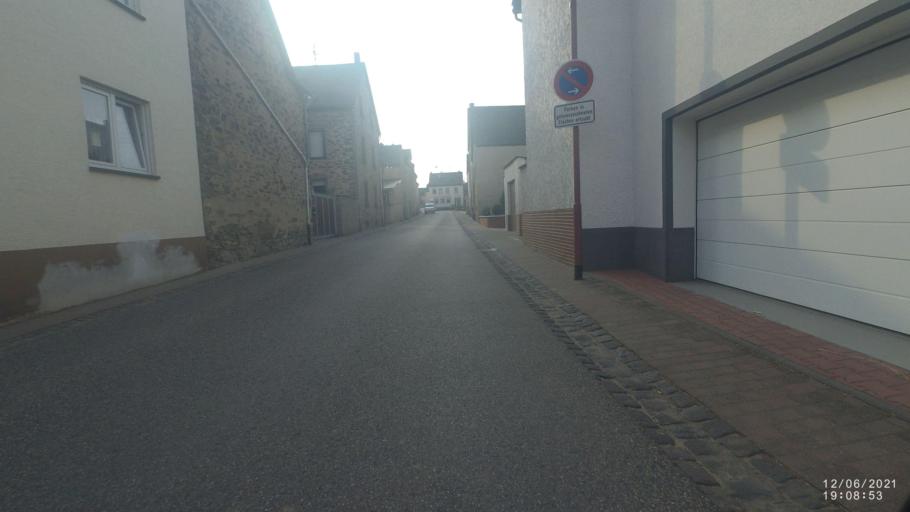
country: DE
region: Rheinland-Pfalz
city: Ruber
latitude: 50.2922
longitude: 7.3748
